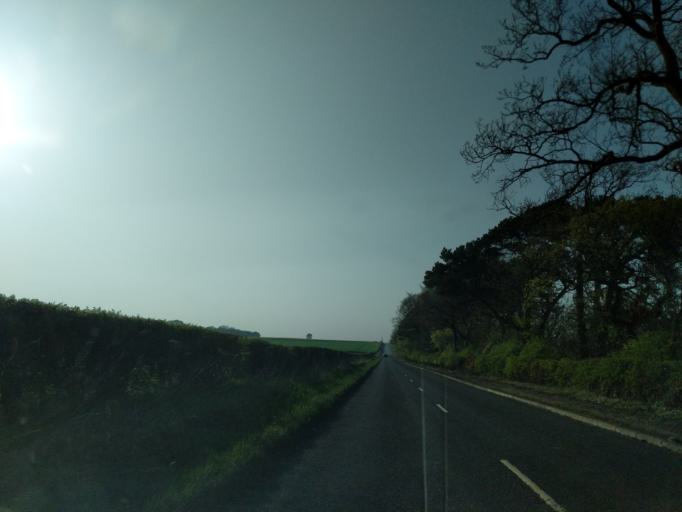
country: GB
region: Scotland
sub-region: Fife
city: Pathhead
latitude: 55.8791
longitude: -3.0122
